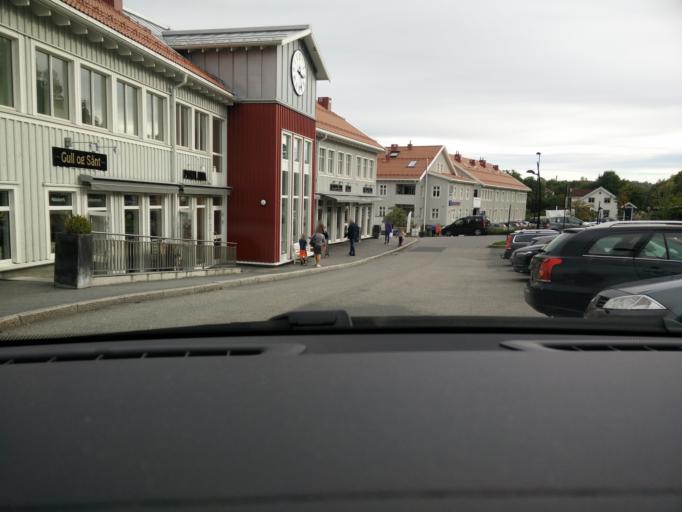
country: NO
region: Akershus
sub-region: Asker
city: Blakstad
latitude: 59.8074
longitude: 10.4857
